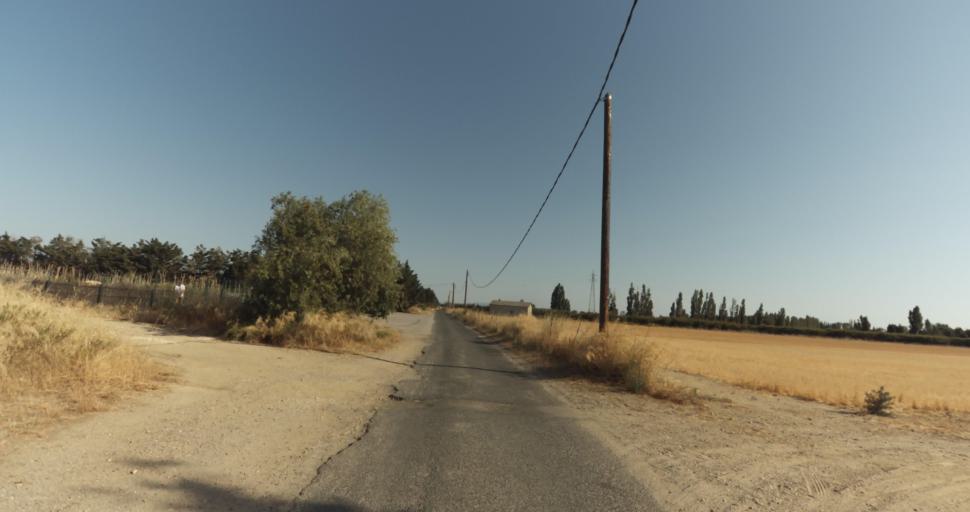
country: FR
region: Languedoc-Roussillon
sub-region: Departement des Pyrenees-Orientales
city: Alenya
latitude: 42.6458
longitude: 2.9770
